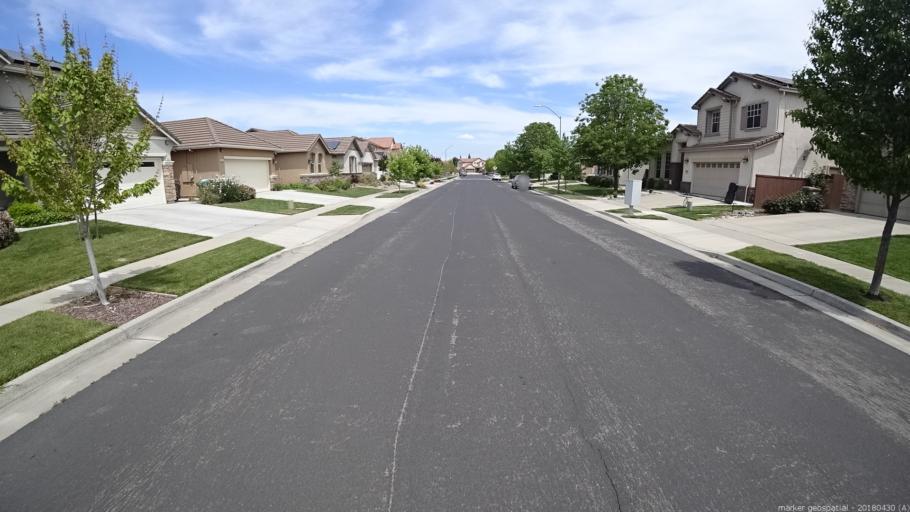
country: US
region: California
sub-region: Yolo County
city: West Sacramento
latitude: 38.5428
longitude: -121.5374
